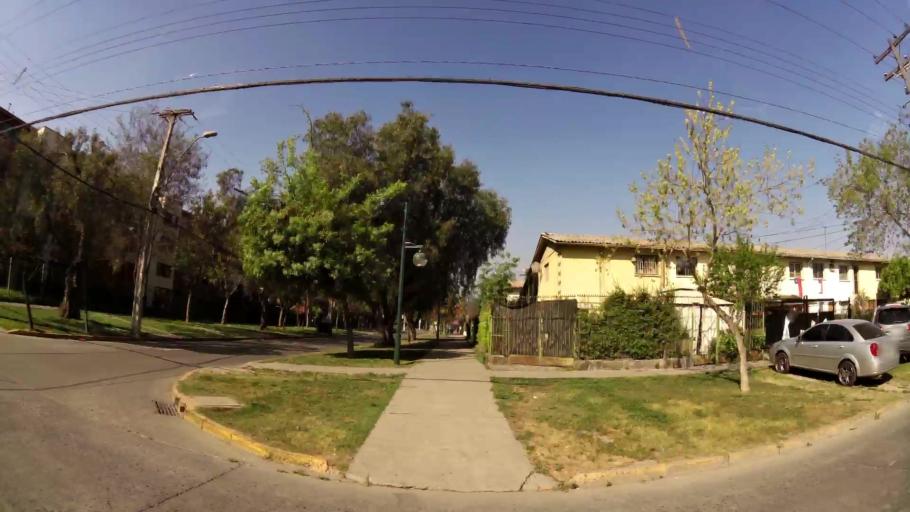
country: CL
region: Santiago Metropolitan
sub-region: Provincia de Santiago
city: Santiago
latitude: -33.4675
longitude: -70.6219
